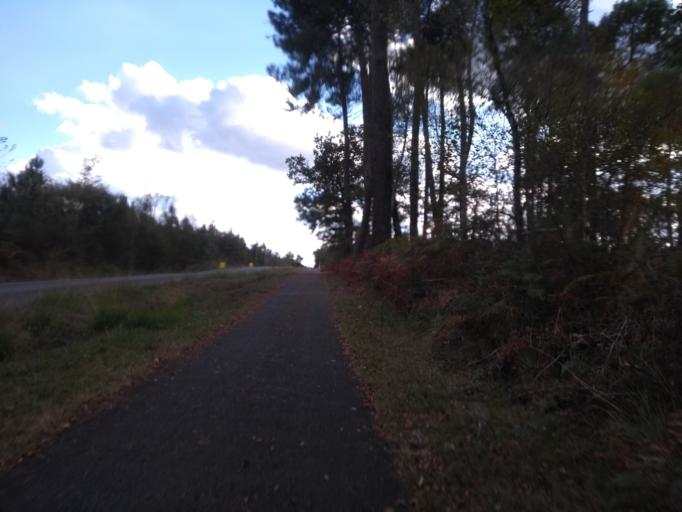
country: FR
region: Aquitaine
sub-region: Departement de la Gironde
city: Cestas
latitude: 44.7305
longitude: -0.6877
